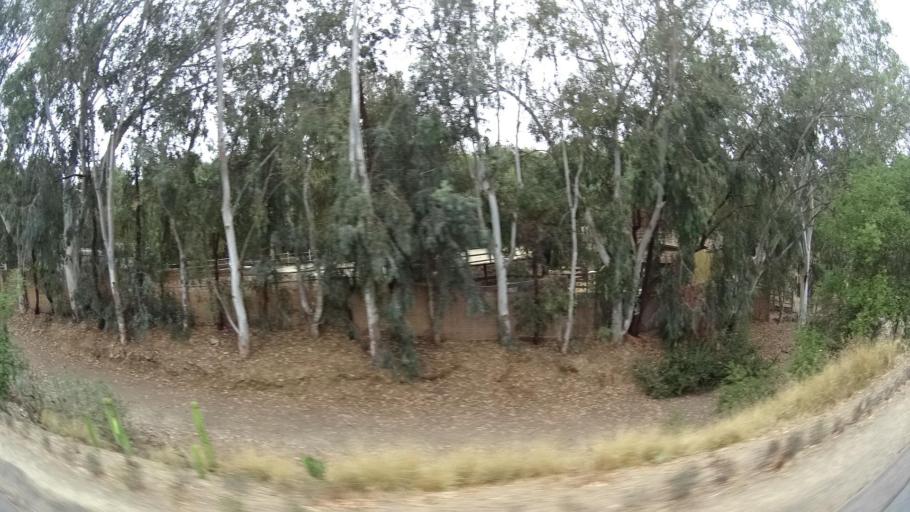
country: US
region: California
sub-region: San Diego County
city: Lake San Marcos
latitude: 33.0822
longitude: -117.1819
